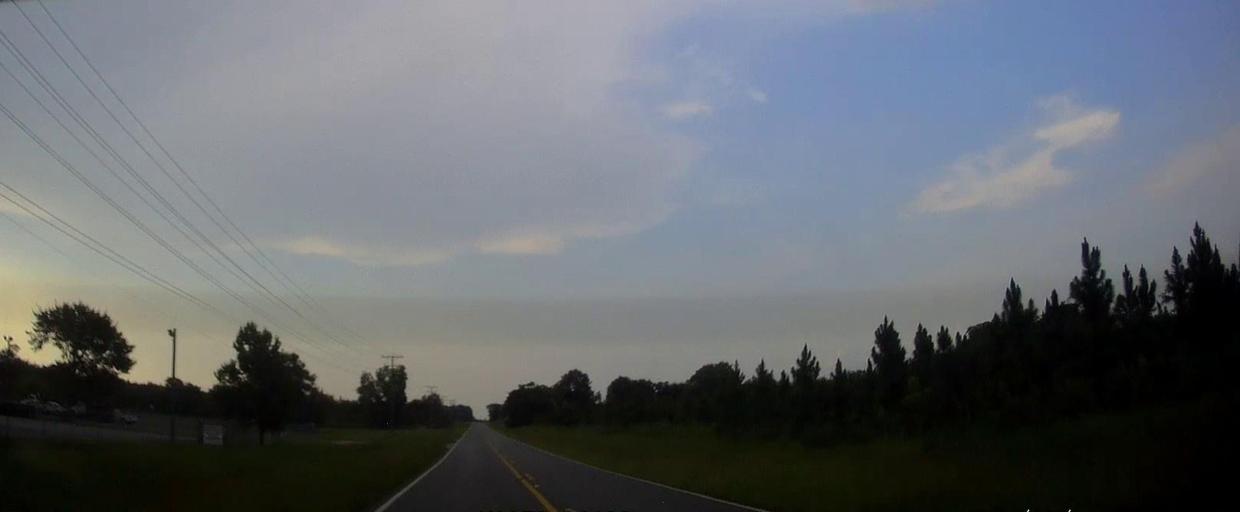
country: US
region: Georgia
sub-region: Laurens County
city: East Dublin
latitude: 32.5482
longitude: -82.8371
